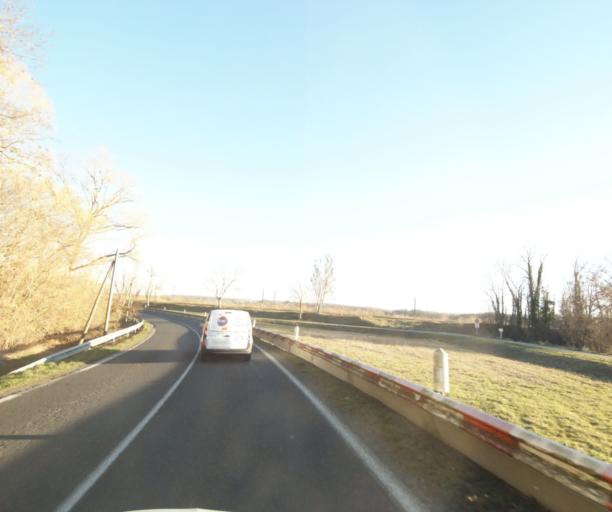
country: FR
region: Lorraine
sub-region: Departement de Meurthe-et-Moselle
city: Art-sur-Meurthe
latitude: 48.6468
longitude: 6.2791
